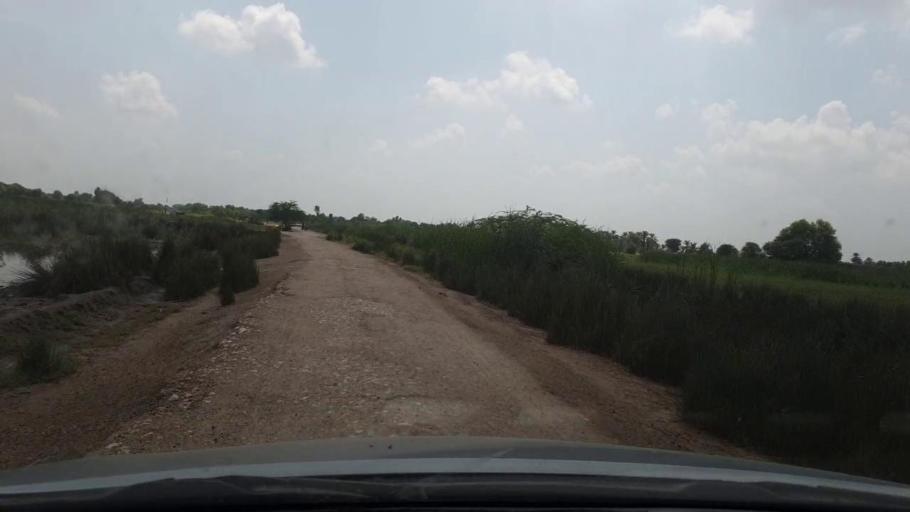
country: PK
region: Sindh
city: Kot Diji
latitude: 27.3979
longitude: 68.7343
